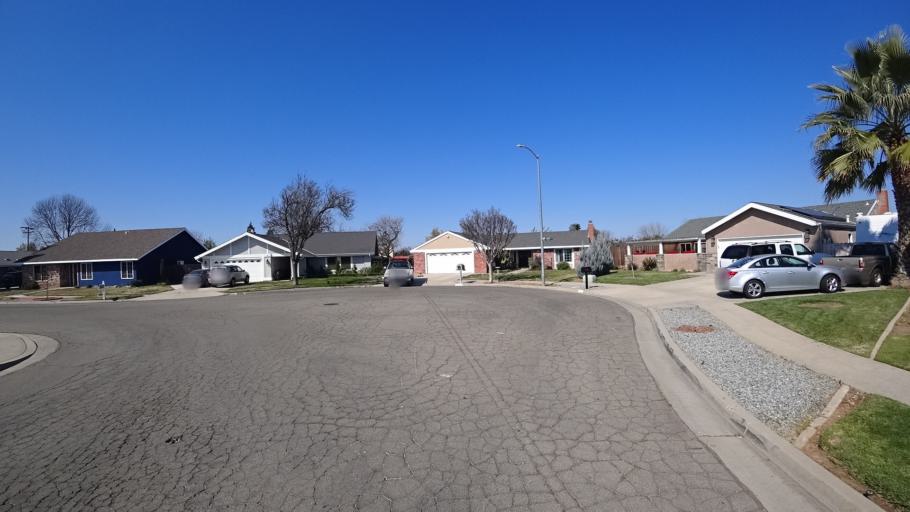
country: US
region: California
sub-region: Fresno County
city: Clovis
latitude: 36.8336
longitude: -119.7333
